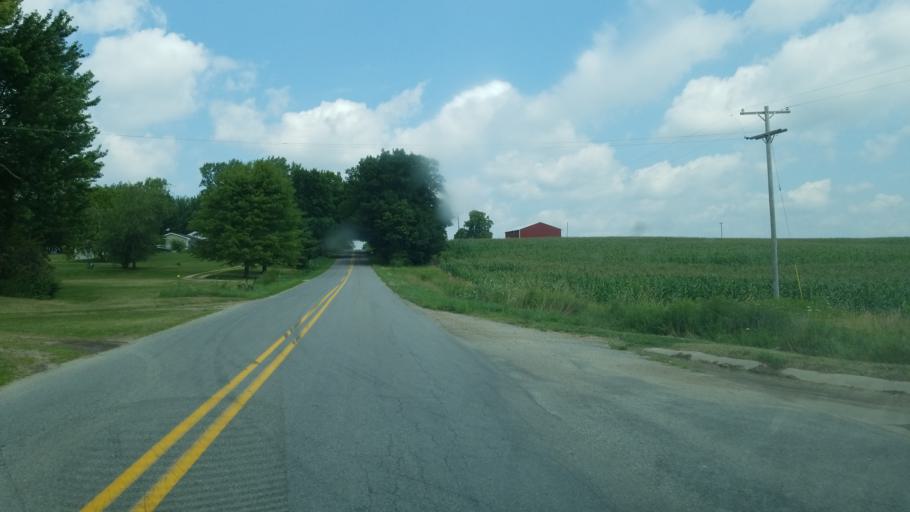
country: US
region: Michigan
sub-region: Kent County
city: Cedar Springs
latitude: 43.2791
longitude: -85.5114
